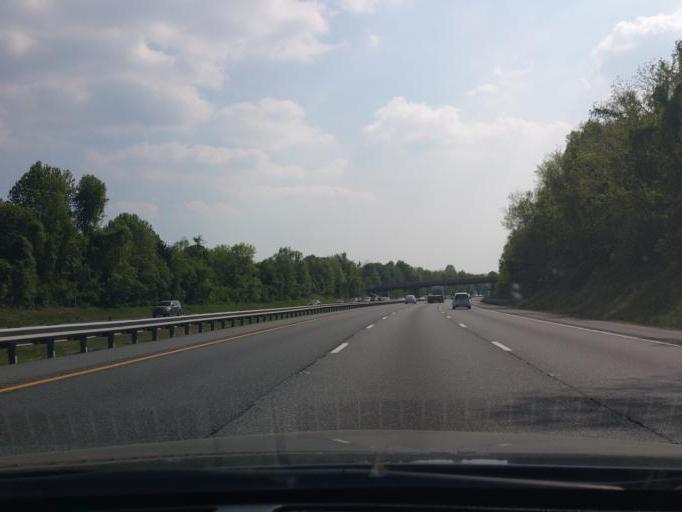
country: US
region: Maryland
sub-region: Harford County
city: Aberdeen
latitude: 39.5367
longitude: -76.1745
